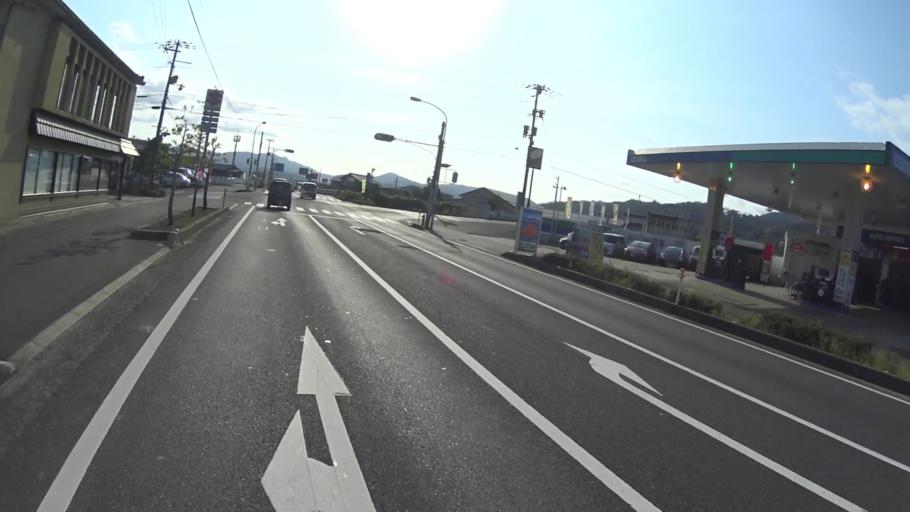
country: JP
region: Kyoto
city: Miyazu
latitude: 35.5374
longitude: 135.1268
